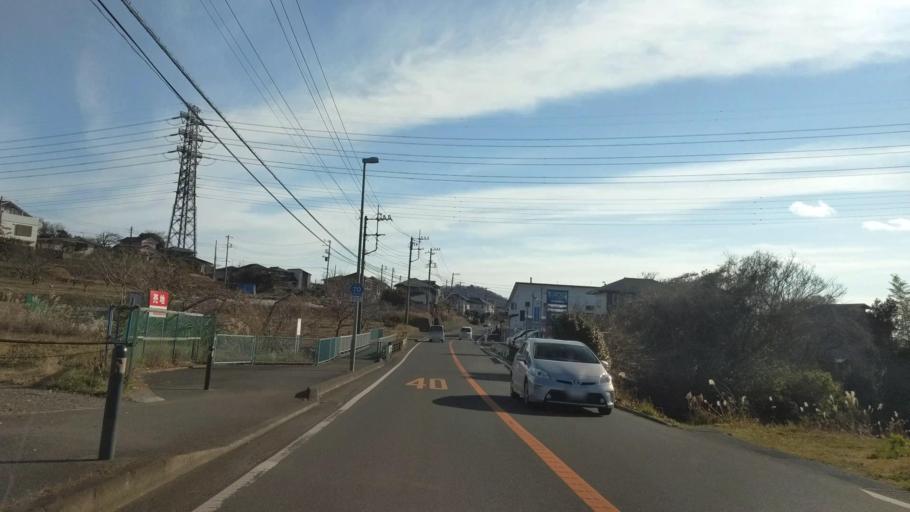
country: JP
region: Kanagawa
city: Hadano
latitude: 35.3900
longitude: 139.2351
